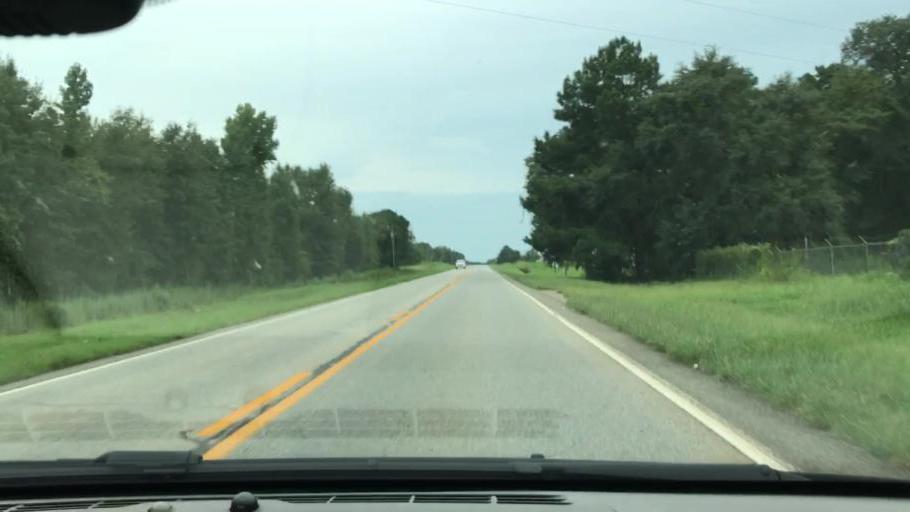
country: US
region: Georgia
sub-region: Early County
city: Blakely
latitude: 31.3445
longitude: -84.9820
